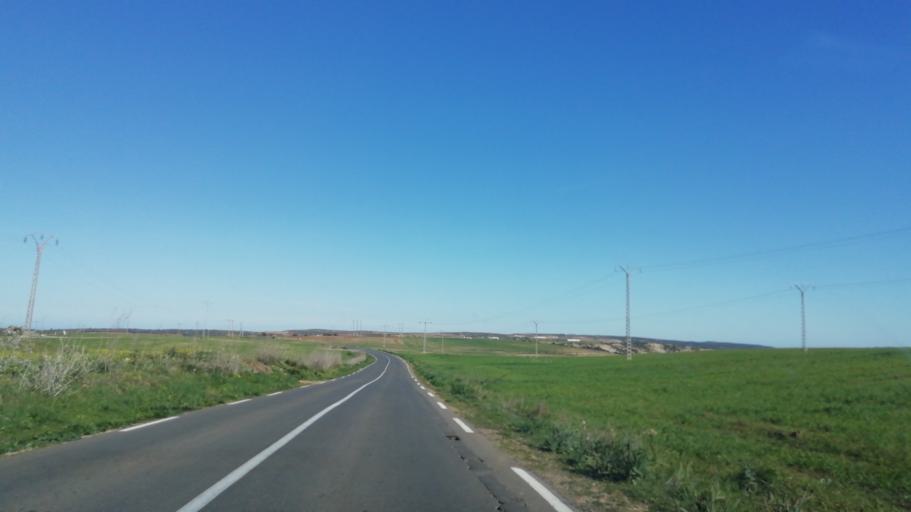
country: DZ
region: Oran
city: Bou Tlelis
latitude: 35.6458
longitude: -0.9462
